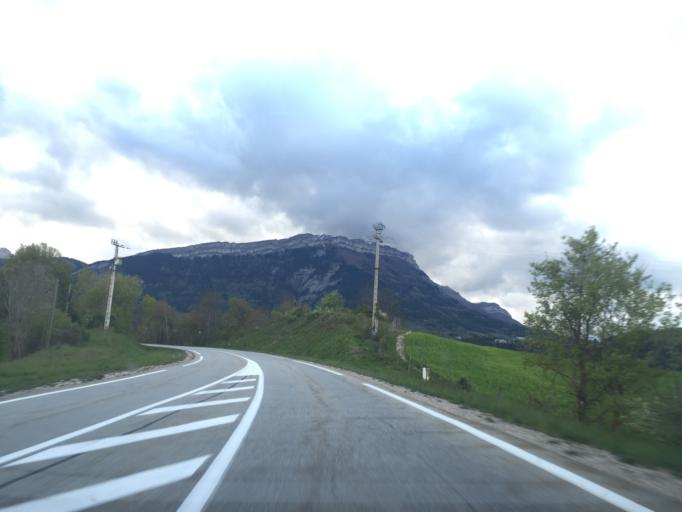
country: FR
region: Rhone-Alpes
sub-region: Departement de l'Isere
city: Mens
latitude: 44.8524
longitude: 5.6203
